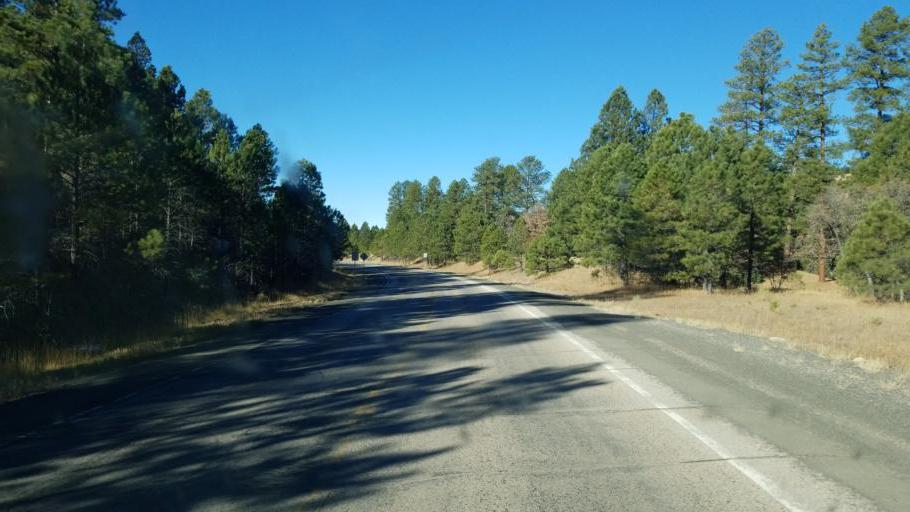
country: US
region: New Mexico
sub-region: McKinley County
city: Navajo
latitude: 36.0764
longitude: -108.9114
